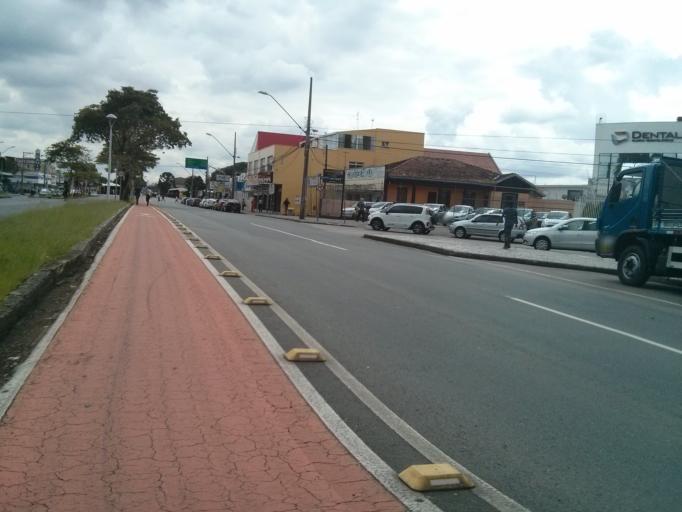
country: BR
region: Parana
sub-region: Sao Jose Dos Pinhais
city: Sao Jose dos Pinhais
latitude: -25.4842
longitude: -49.2459
